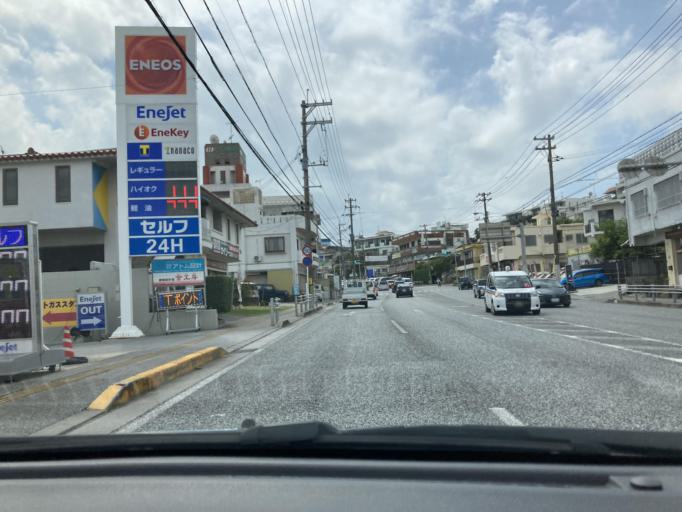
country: JP
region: Okinawa
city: Okinawa
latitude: 26.3232
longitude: 127.8221
